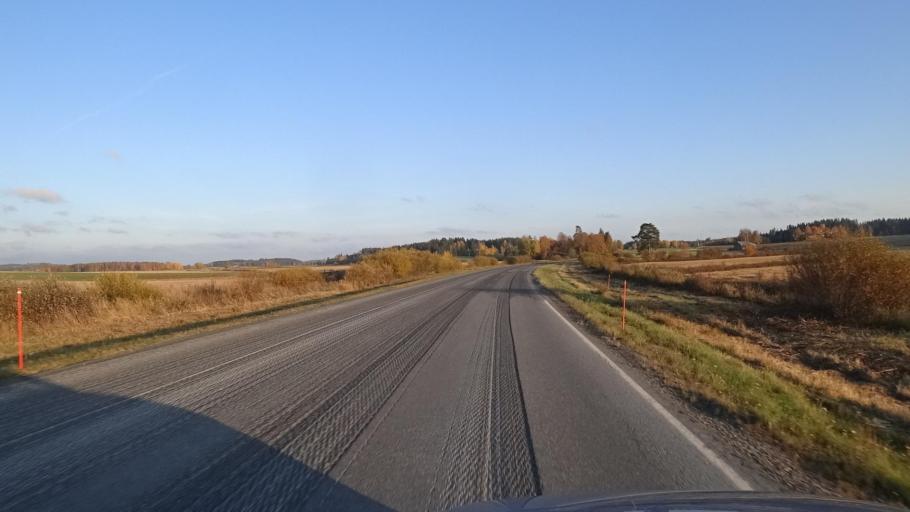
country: FI
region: Haeme
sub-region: Forssa
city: Ypaejae
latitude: 60.7856
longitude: 23.3007
